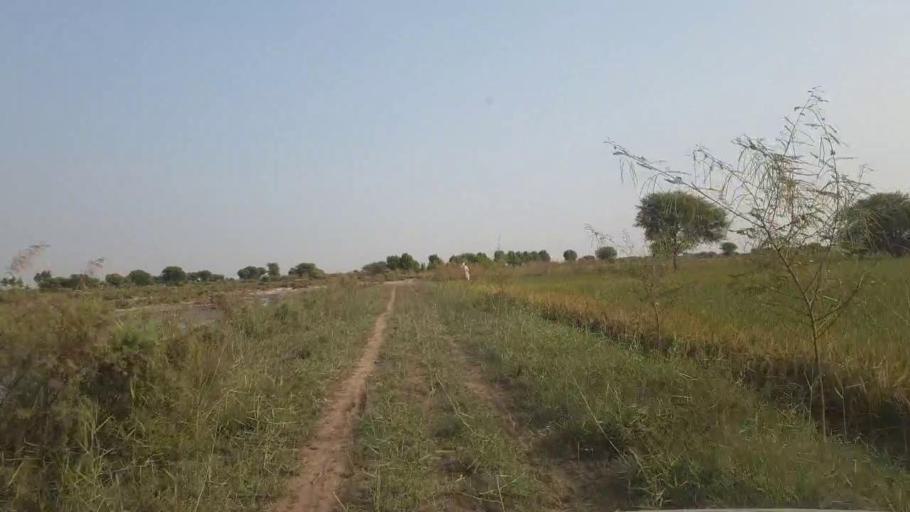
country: PK
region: Sindh
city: Matli
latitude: 25.0469
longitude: 68.7513
